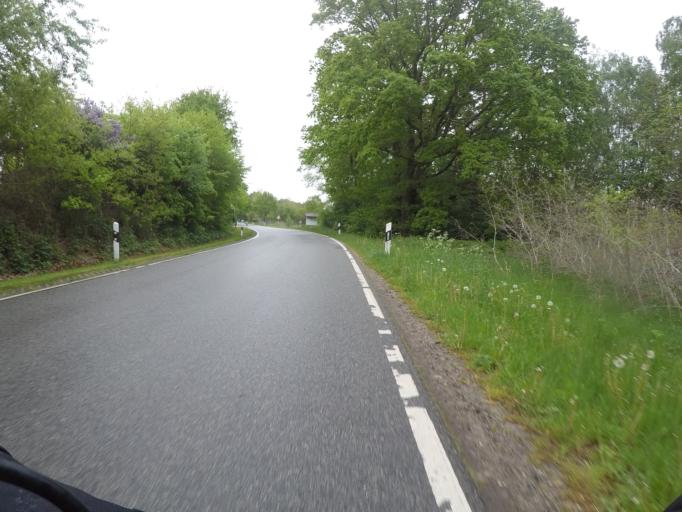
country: DE
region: Schleswig-Holstein
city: Rickling
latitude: 53.9814
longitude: 10.1404
